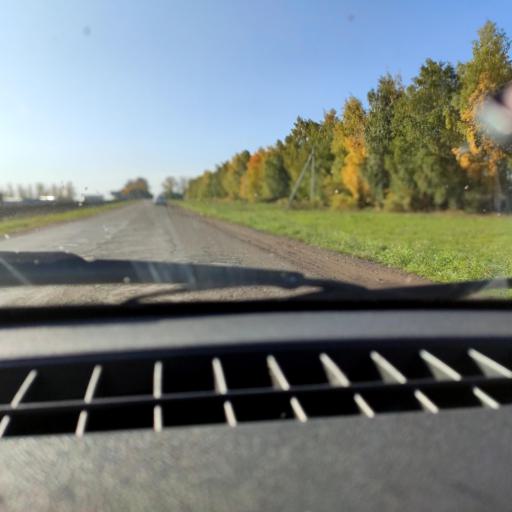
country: RU
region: Bashkortostan
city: Avdon
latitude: 54.5932
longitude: 55.8002
